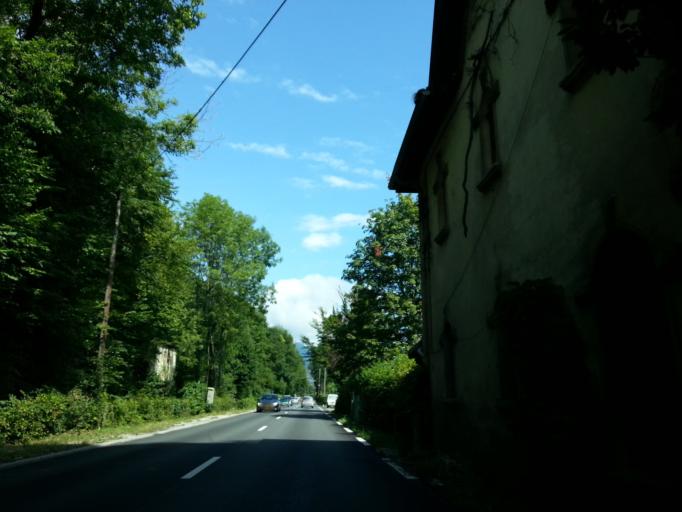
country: FR
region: Rhone-Alpes
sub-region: Departement de la Haute-Savoie
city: Doussard
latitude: 45.8027
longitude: 6.2123
